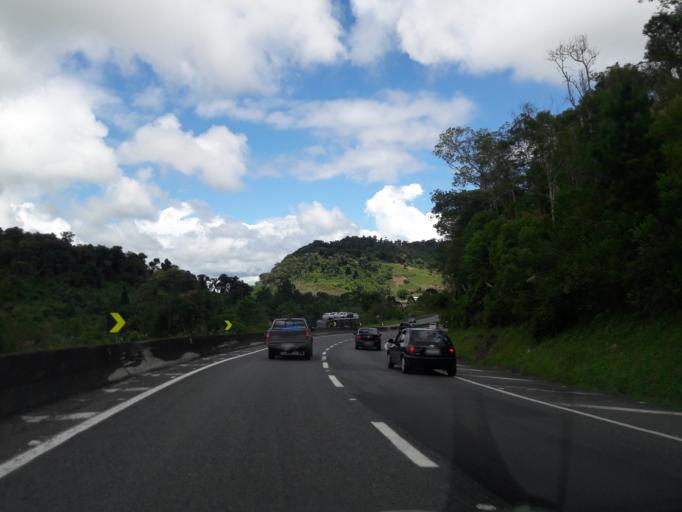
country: BR
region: Parana
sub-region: Antonina
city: Antonina
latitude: -25.0245
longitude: -48.5183
